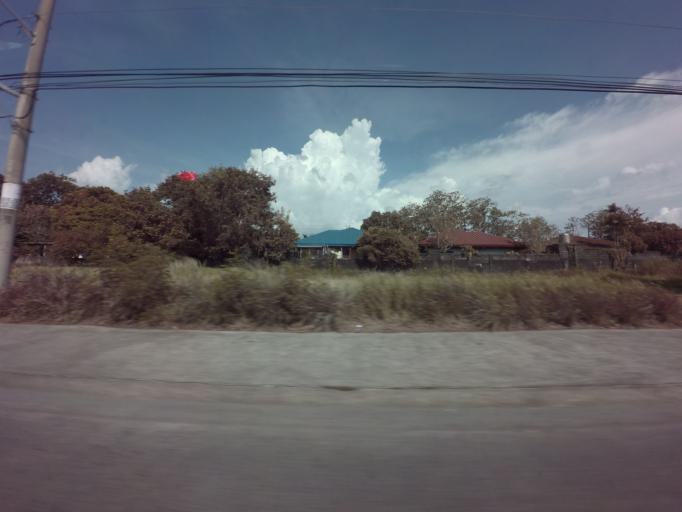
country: PH
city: Sambayanihan People's Village
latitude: 14.4410
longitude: 121.0059
